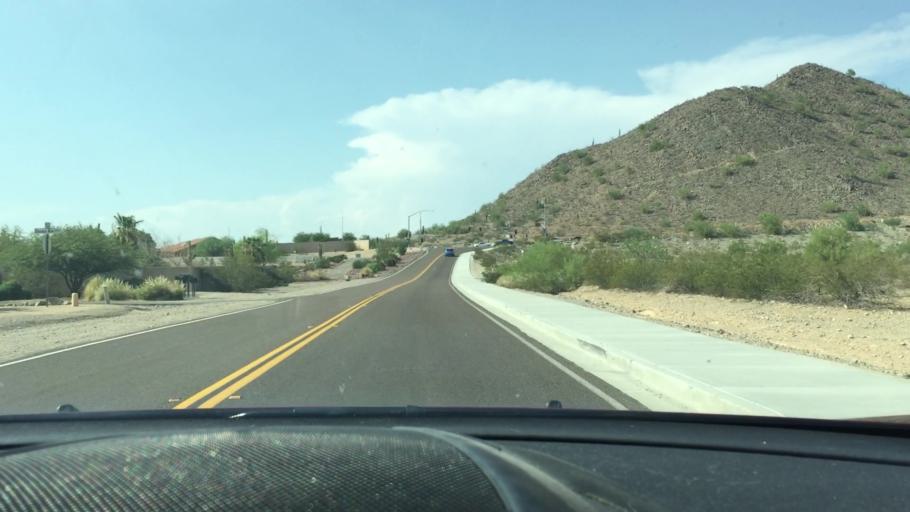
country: US
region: Arizona
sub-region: Maricopa County
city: Sun City West
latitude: 33.7082
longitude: -112.2549
